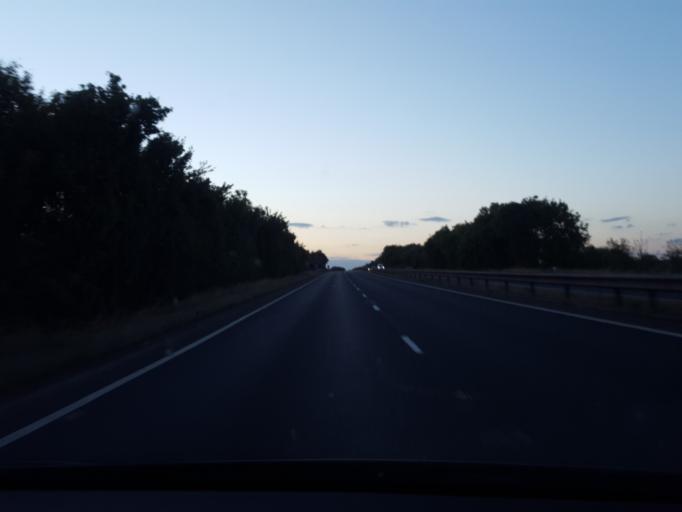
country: GB
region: England
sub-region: Leicestershire
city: Mountsorrel
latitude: 52.7298
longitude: -1.1329
